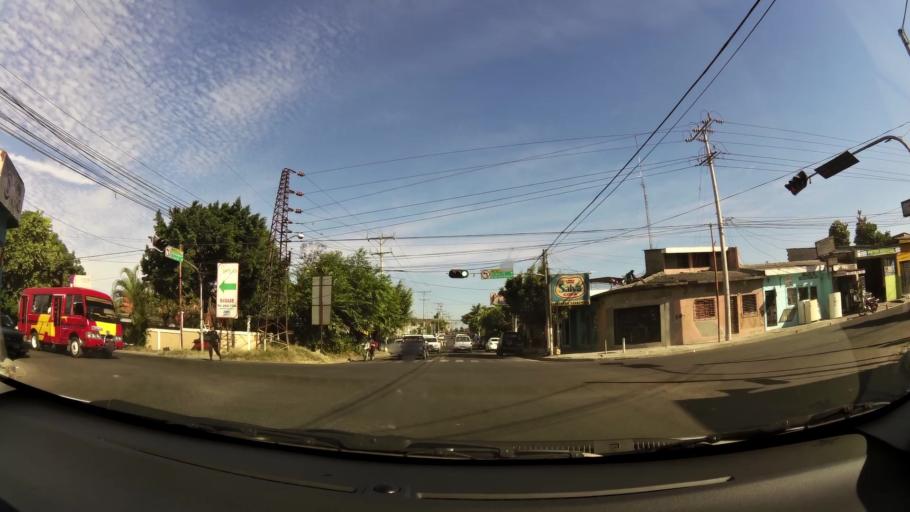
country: SV
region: Santa Ana
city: Santa Ana
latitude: 13.9842
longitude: -89.5664
